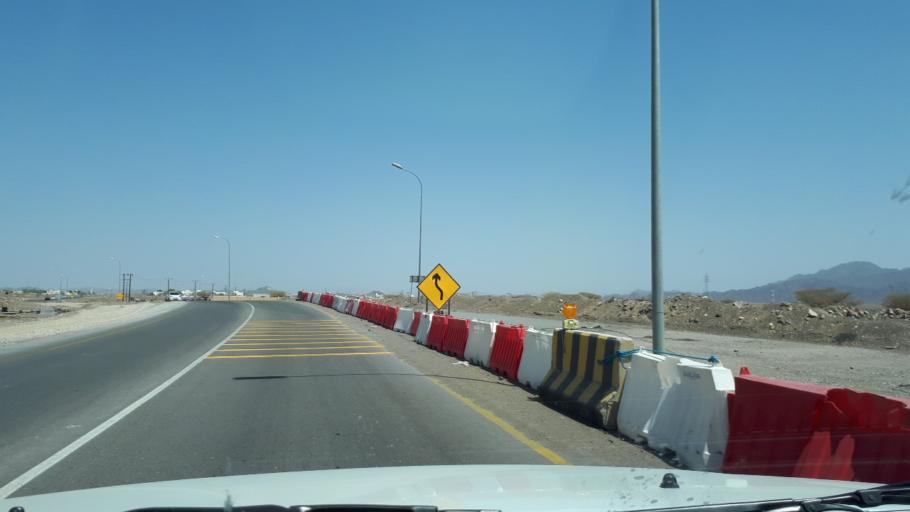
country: OM
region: Ash Sharqiyah
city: Al Qabil
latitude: 22.5715
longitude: 58.6980
